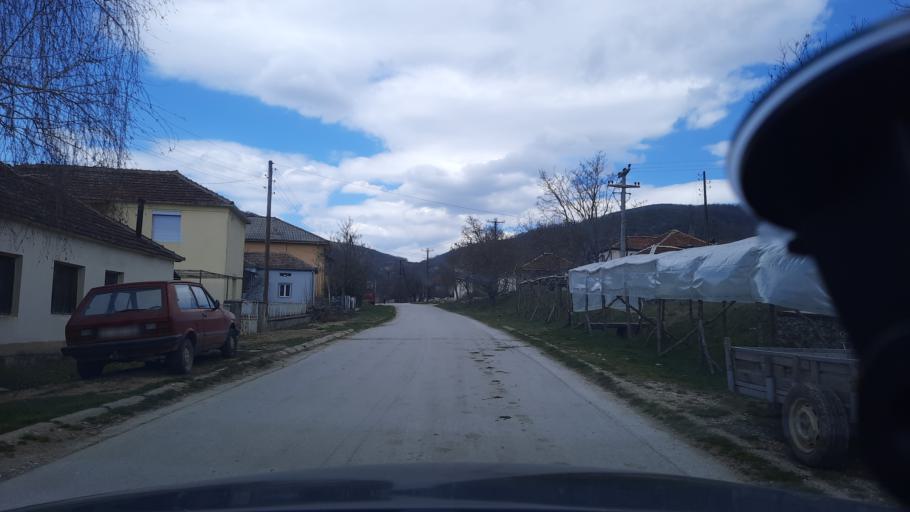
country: MK
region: Demir Hisar
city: Sopotnica
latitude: 41.2941
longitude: 21.1561
